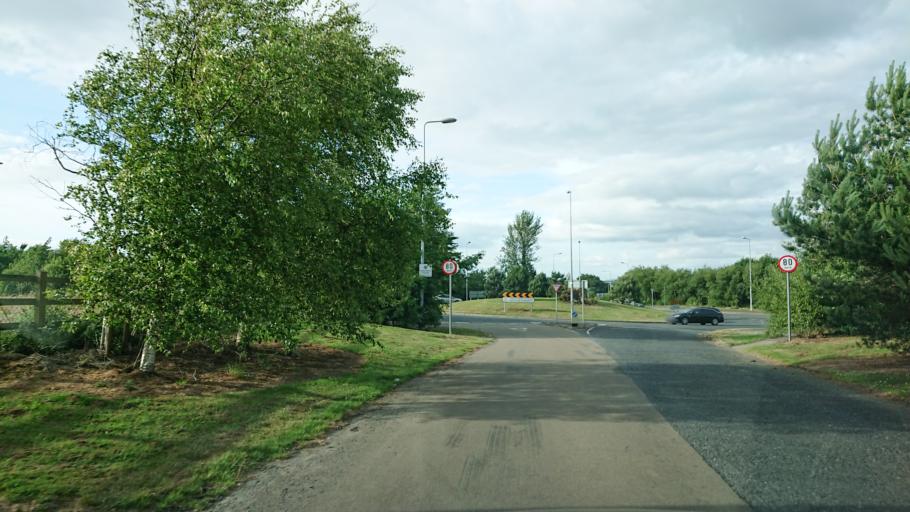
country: IE
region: Munster
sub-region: Waterford
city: Waterford
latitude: 52.2365
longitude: -7.1575
